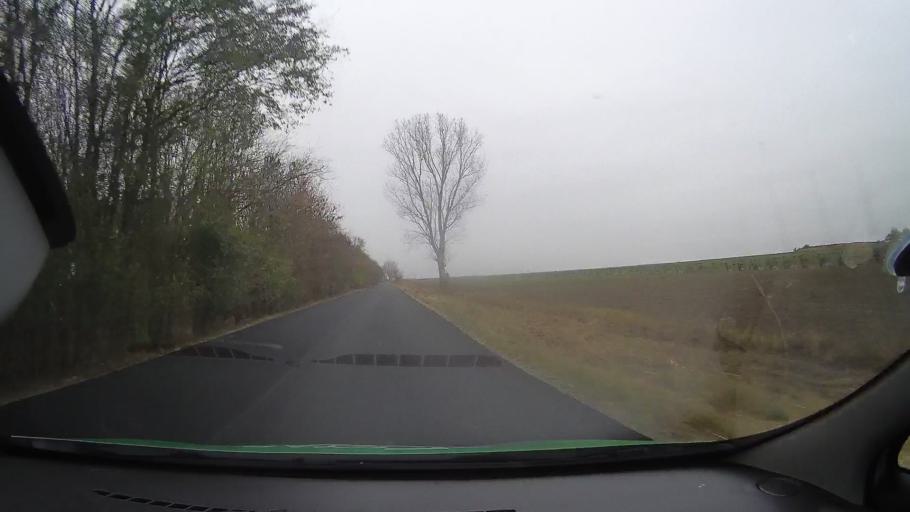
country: RO
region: Ialomita
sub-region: Comuna Valea Ciorii
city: Valea Ciorii
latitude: 44.7436
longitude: 27.5745
